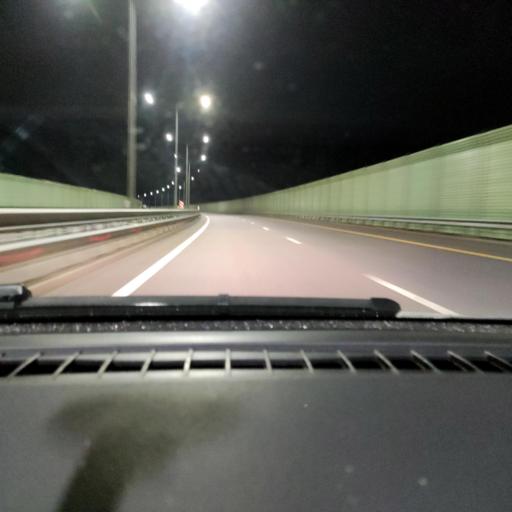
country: RU
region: Voronezj
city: Novaya Usman'
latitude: 51.6129
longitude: 39.3193
